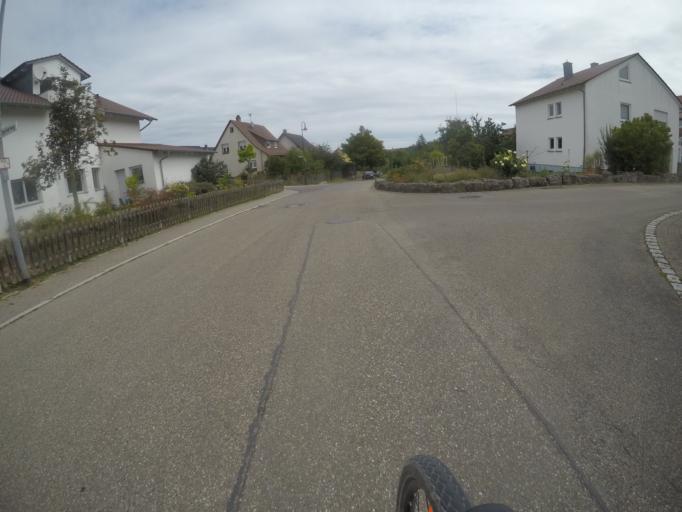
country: DE
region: Baden-Wuerttemberg
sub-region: Karlsruhe Region
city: Muhlacker
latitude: 48.9402
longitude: 8.8316
